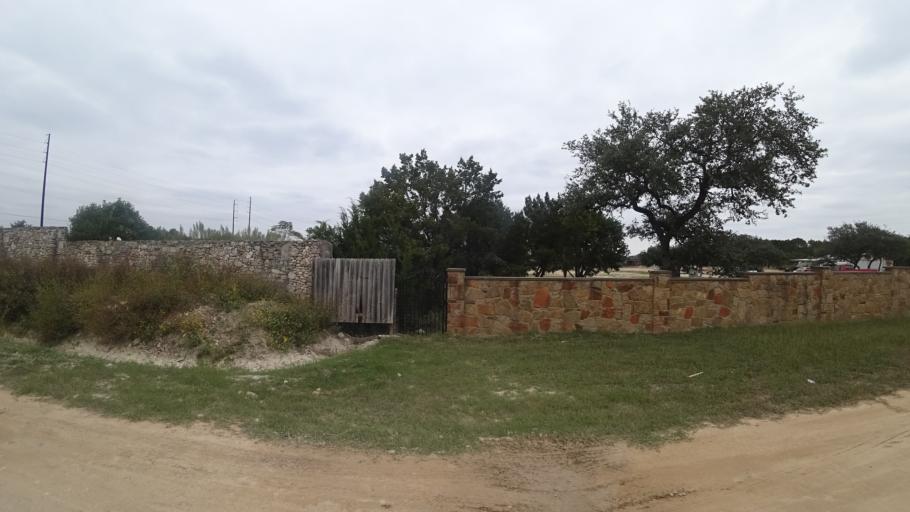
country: US
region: Texas
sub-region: Travis County
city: Lakeway
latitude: 30.3734
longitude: -97.9431
